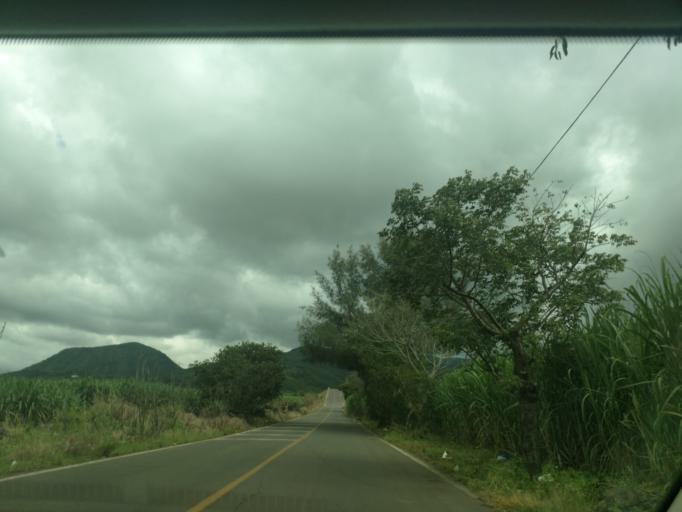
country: MX
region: Nayarit
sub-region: Tepic
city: La Corregidora
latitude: 21.4536
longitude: -104.8082
